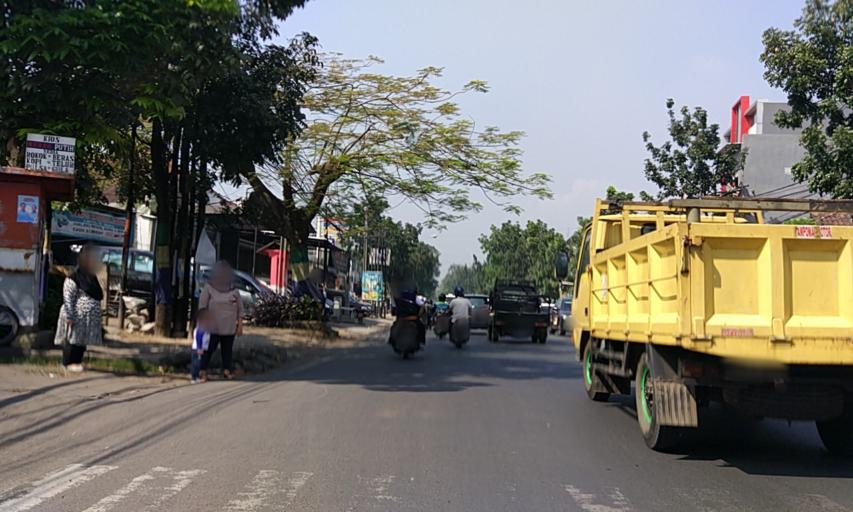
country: ID
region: West Java
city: Bandung
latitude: -6.9399
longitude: 107.6065
